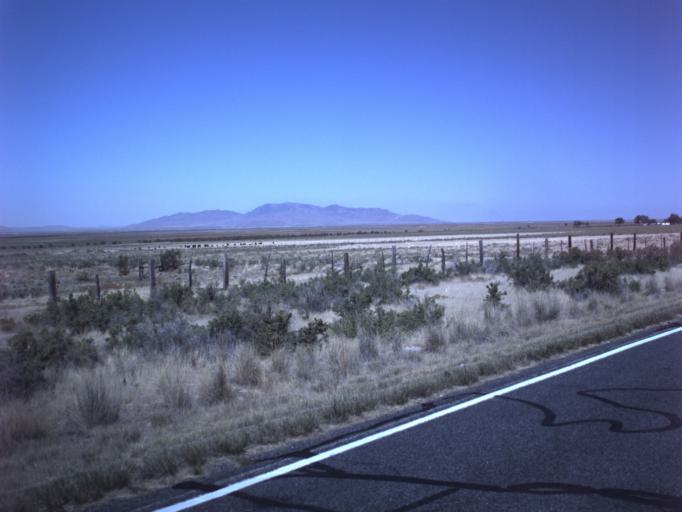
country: US
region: Utah
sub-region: Tooele County
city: Grantsville
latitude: 40.6220
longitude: -112.6998
